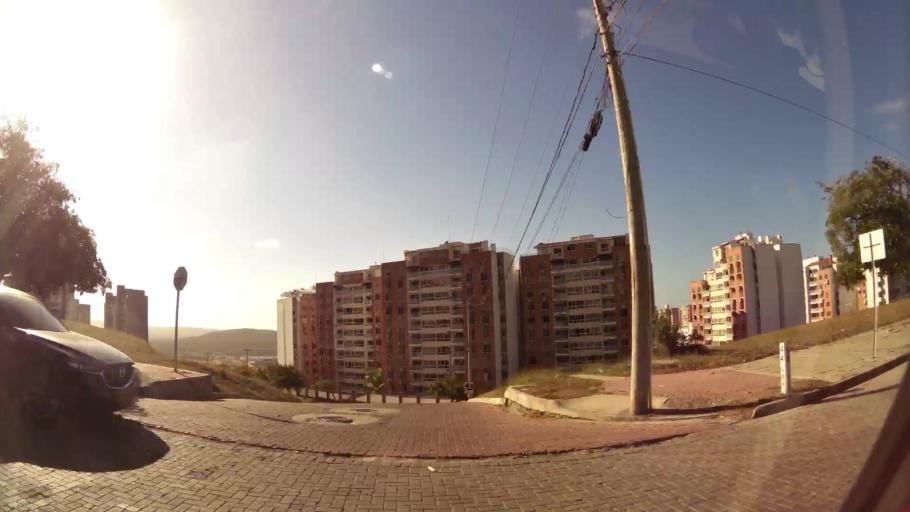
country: CO
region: Atlantico
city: Barranquilla
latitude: 11.0050
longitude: -74.8335
